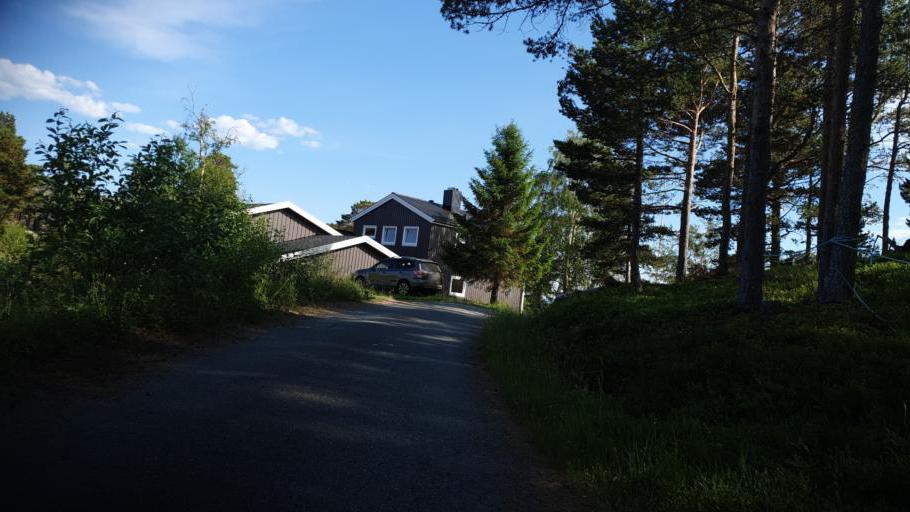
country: NO
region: Sor-Trondelag
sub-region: Trondheim
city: Trondheim
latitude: 63.5727
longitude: 10.4196
